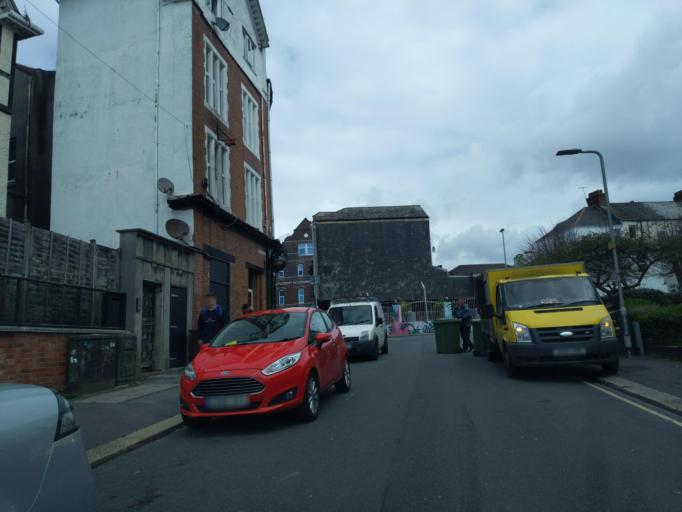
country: GB
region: England
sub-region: Plymouth
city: Plymouth
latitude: 50.3766
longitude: -4.1377
